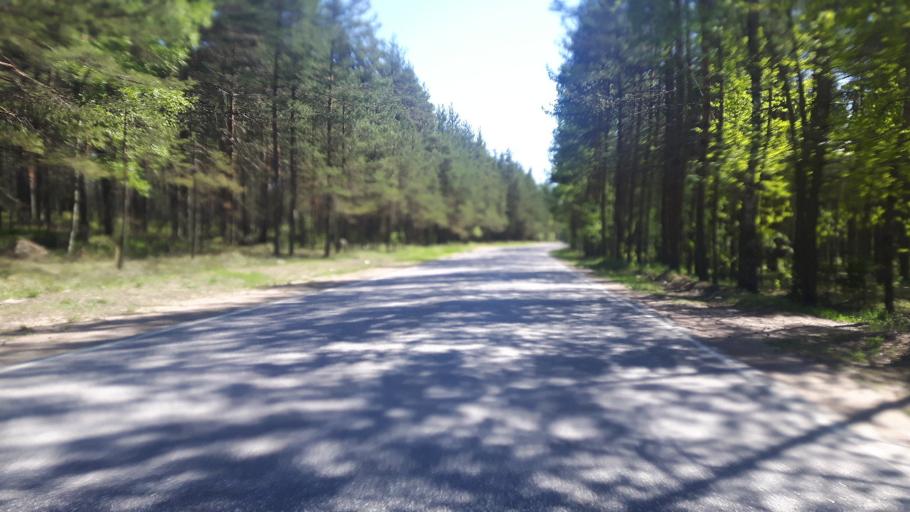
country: RU
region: Leningrad
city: Glebychevo
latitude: 60.3473
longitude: 28.8198
